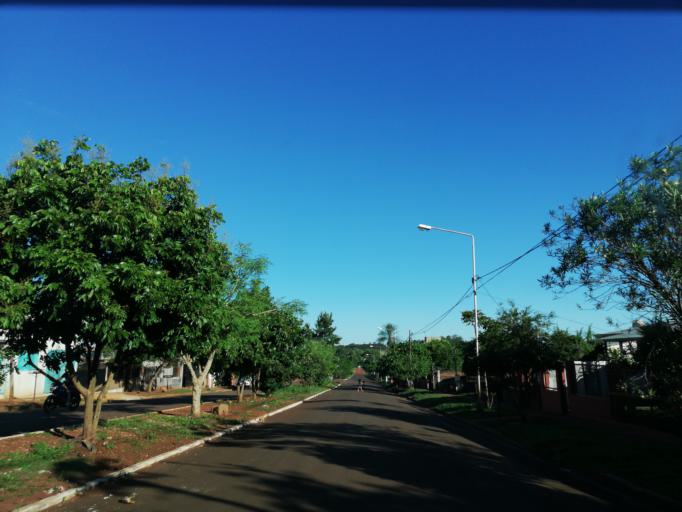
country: AR
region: Misiones
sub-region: Departamento de Capital
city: Posadas
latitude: -27.4357
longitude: -55.9399
